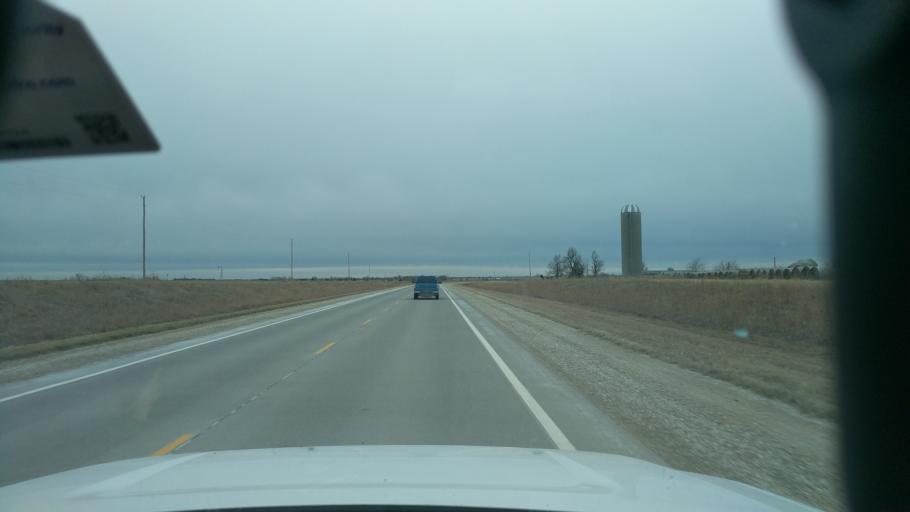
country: US
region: Kansas
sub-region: Dickinson County
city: Herington
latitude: 38.5774
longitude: -96.9481
